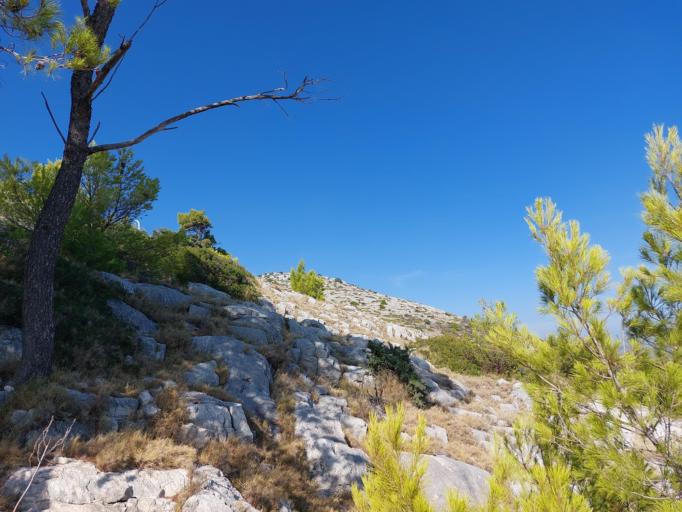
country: HR
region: Dubrovacko-Neretvanska
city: Smokvica
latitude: 42.7340
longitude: 16.8405
